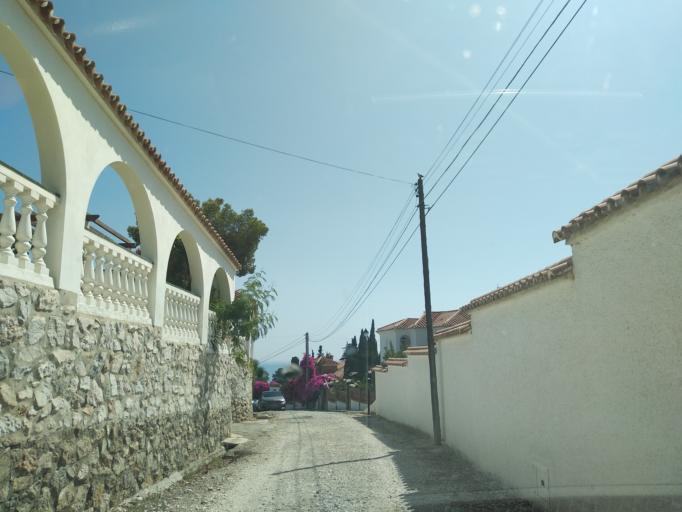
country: ES
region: Andalusia
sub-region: Provincia de Malaga
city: Valdes
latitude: 36.7185
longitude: -4.2014
